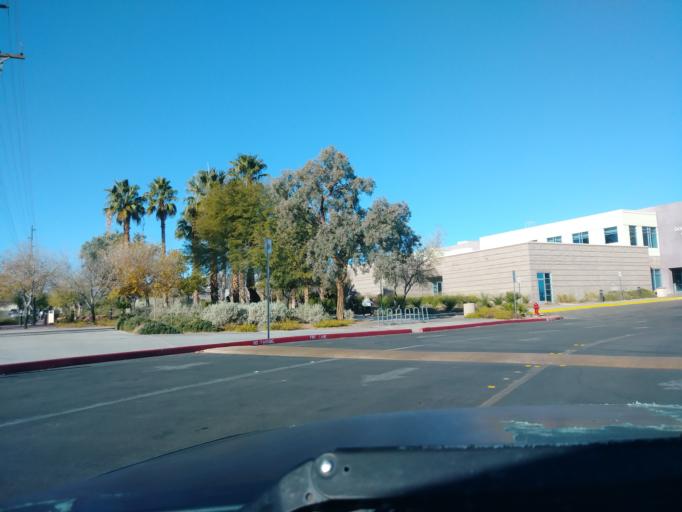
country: US
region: Nevada
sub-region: Clark County
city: Spring Valley
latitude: 36.1574
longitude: -115.2323
